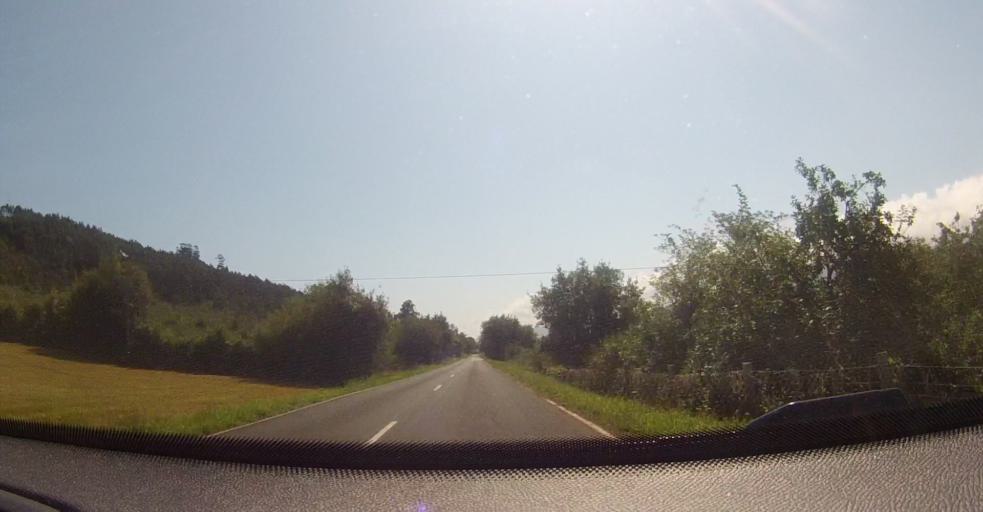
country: ES
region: Asturias
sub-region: Province of Asturias
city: Colunga
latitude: 43.4883
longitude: -5.3034
